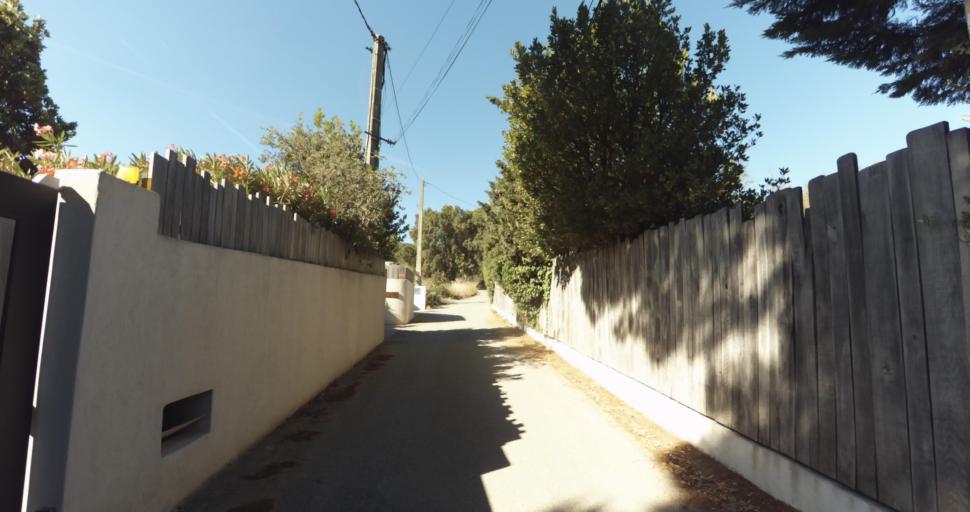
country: FR
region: Provence-Alpes-Cote d'Azur
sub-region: Departement du Var
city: Saint-Tropez
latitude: 43.2605
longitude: 6.6204
